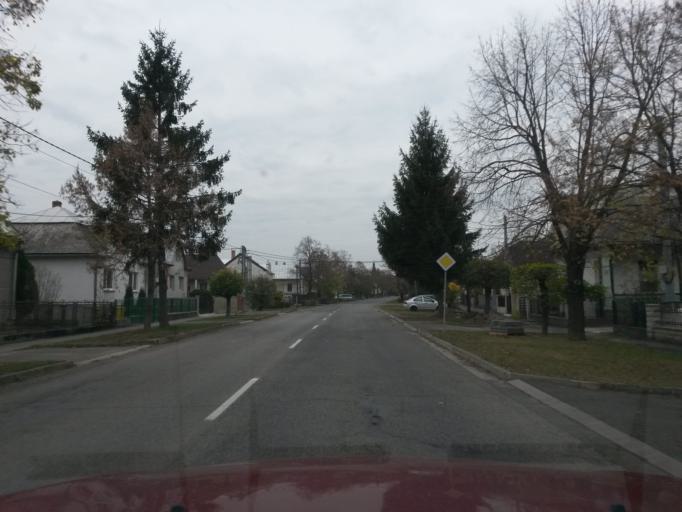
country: SK
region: Kosicky
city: Trebisov
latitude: 48.6458
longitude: 21.6801
